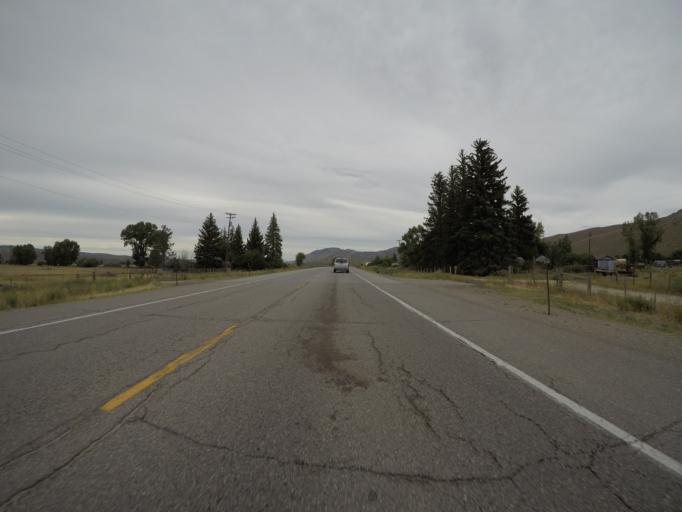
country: US
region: Idaho
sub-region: Bear Lake County
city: Montpelier
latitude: 42.0954
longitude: -110.9516
